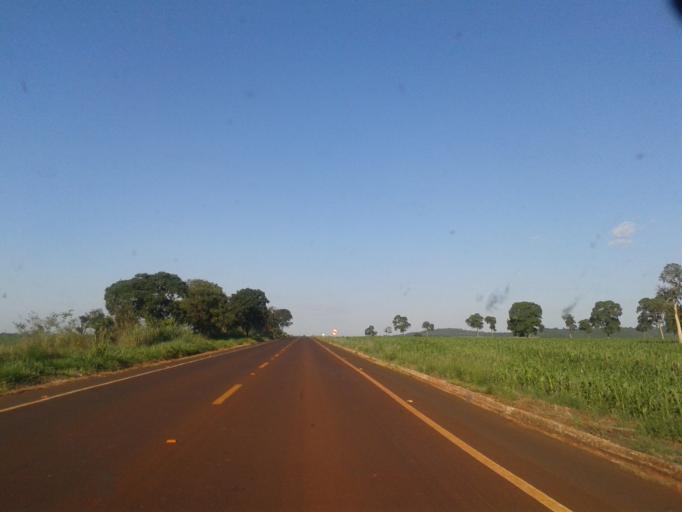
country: BR
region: Minas Gerais
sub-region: Capinopolis
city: Capinopolis
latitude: -18.7122
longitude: -49.8366
